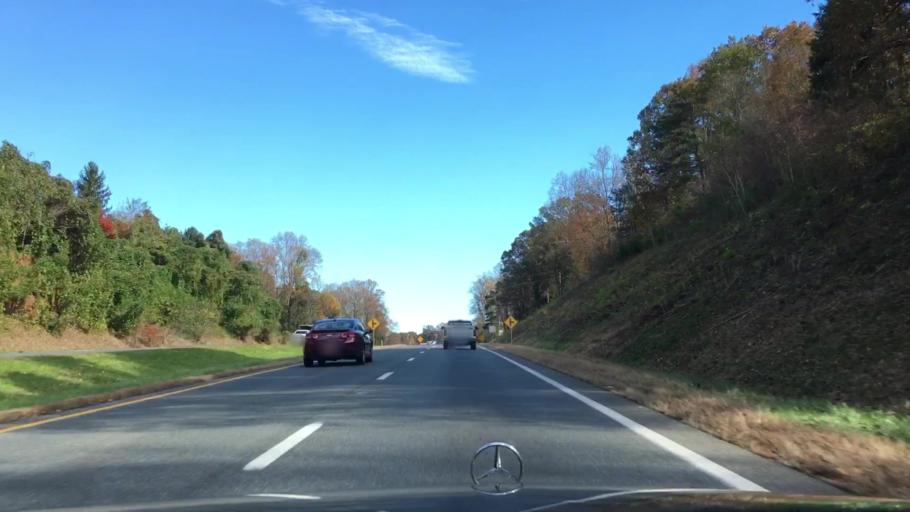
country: US
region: Virginia
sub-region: Campbell County
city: Altavista
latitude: 37.1455
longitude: -79.2347
